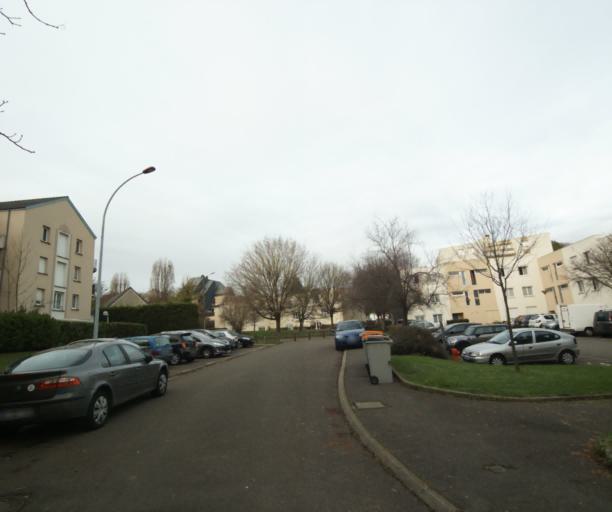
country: FR
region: Pays de la Loire
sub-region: Departement de la Sarthe
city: Le Mans
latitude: 48.0005
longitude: 0.2279
